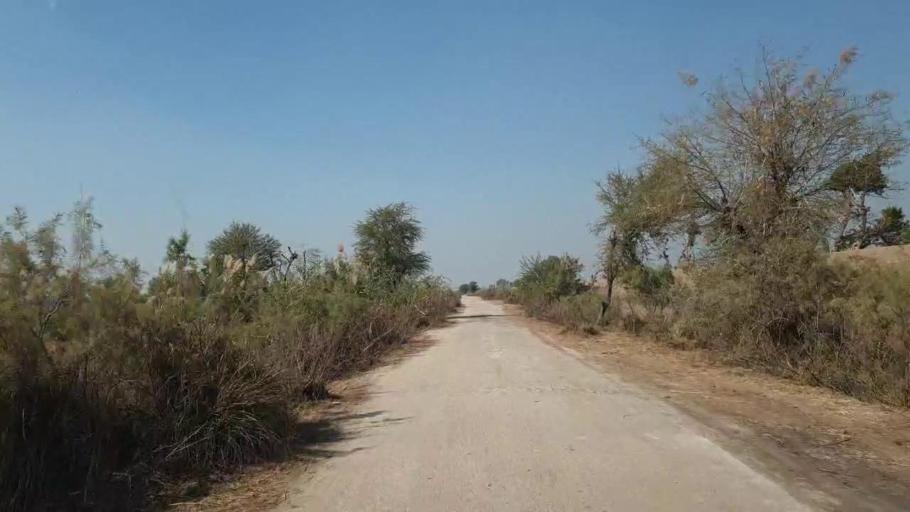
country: PK
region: Sindh
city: Bhit Shah
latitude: 25.9152
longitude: 68.5029
